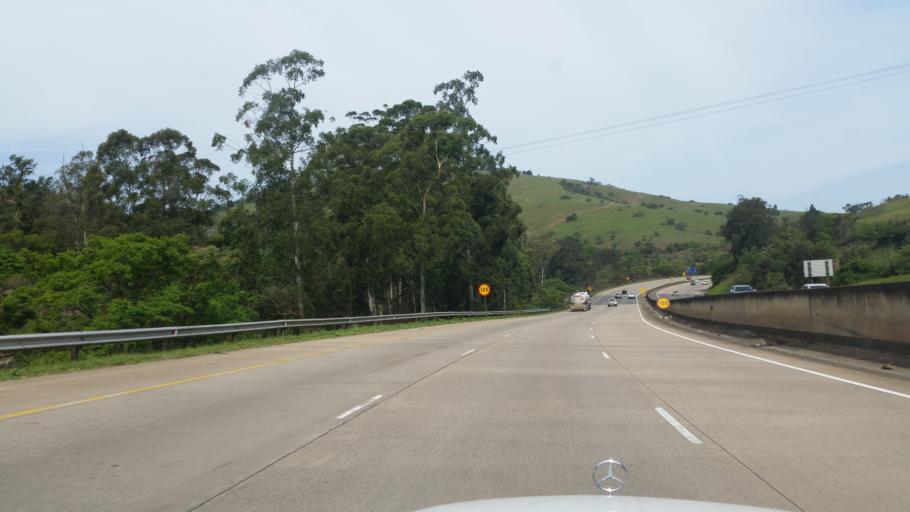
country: ZA
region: KwaZulu-Natal
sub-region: eThekwini Metropolitan Municipality
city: Mpumalanga
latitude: -29.7412
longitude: 30.6602
